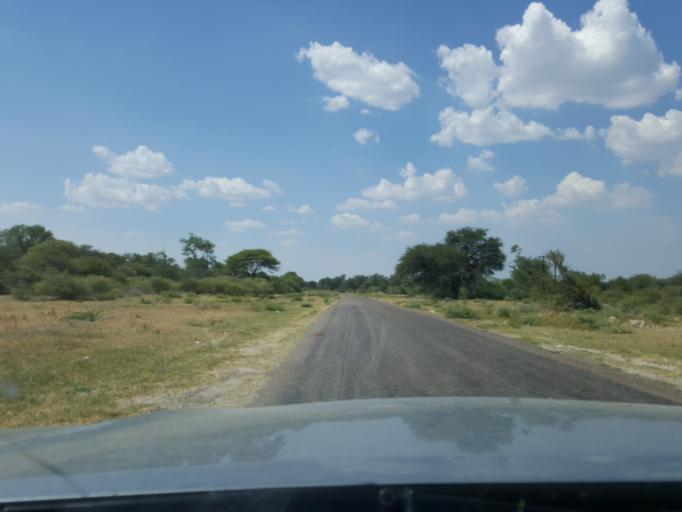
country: BW
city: Nokaneng
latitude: -19.4368
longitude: 22.1317
